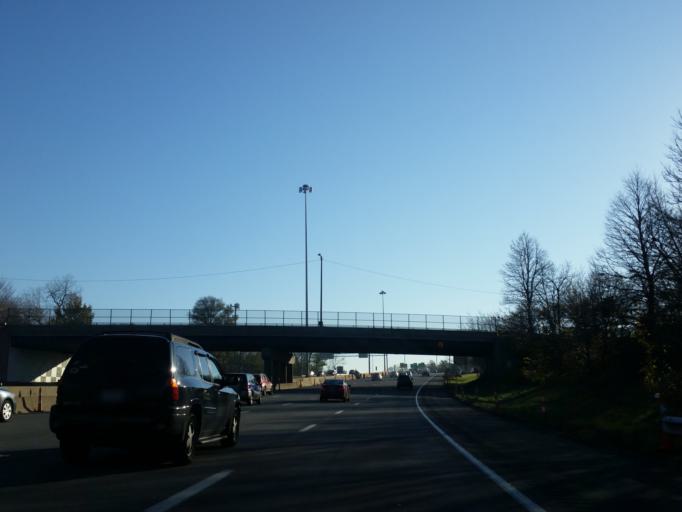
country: US
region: Ohio
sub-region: Cuyahoga County
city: Cleveland
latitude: 41.4749
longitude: -81.7145
